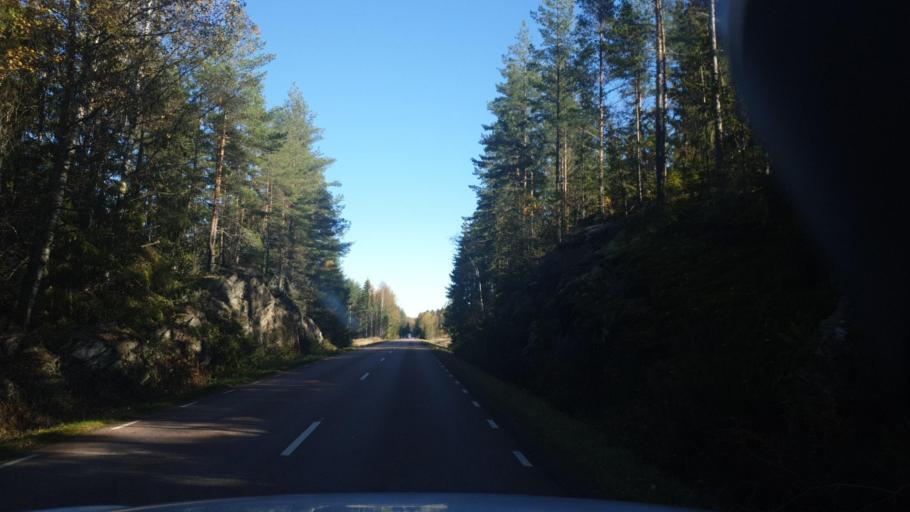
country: SE
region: Vaermland
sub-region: Grums Kommun
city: Grums
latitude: 59.3997
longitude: 13.0269
